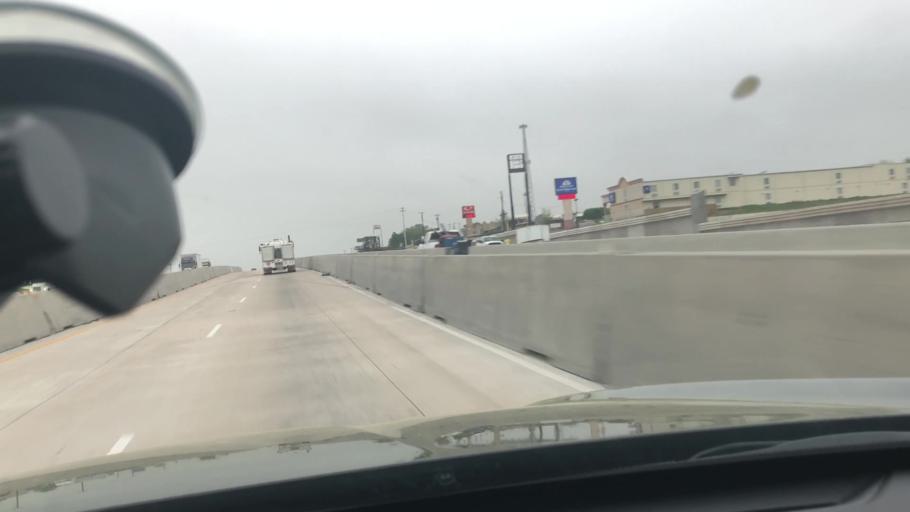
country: US
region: Texas
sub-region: Bell County
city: Temple
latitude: 31.1093
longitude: -97.3571
